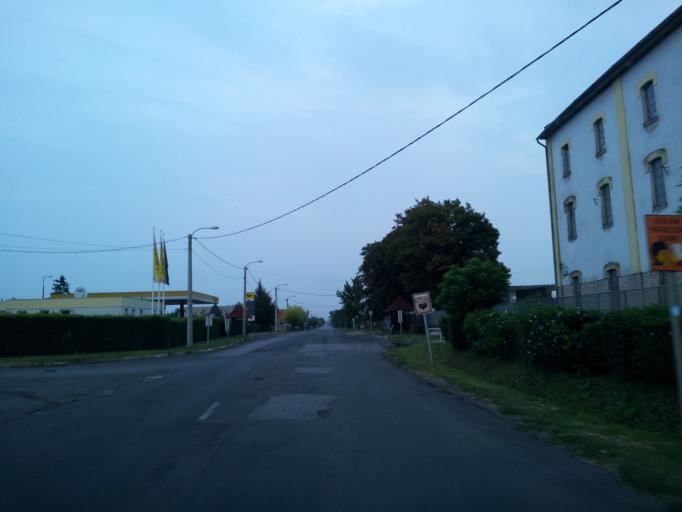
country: HU
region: Tolna
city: Tolna
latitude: 46.4137
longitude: 18.7498
